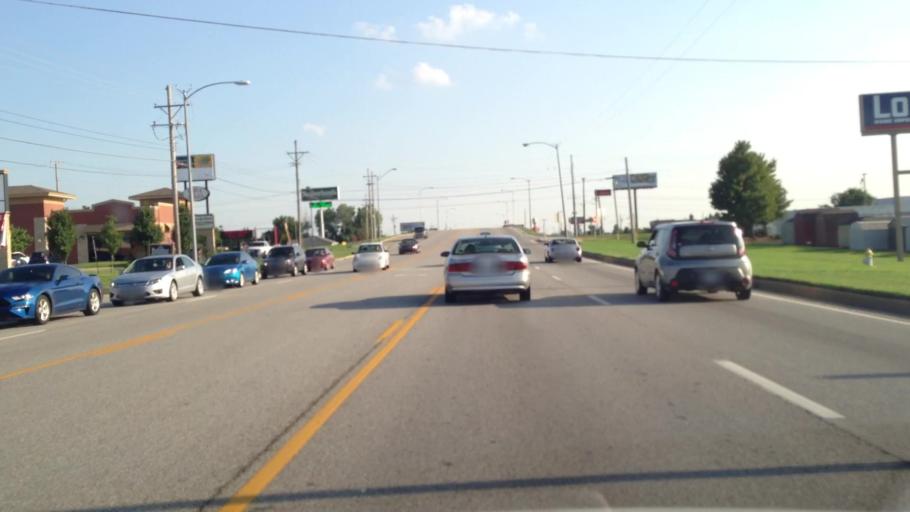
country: US
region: Missouri
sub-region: Jasper County
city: Duquesne
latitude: 37.0607
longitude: -94.4770
